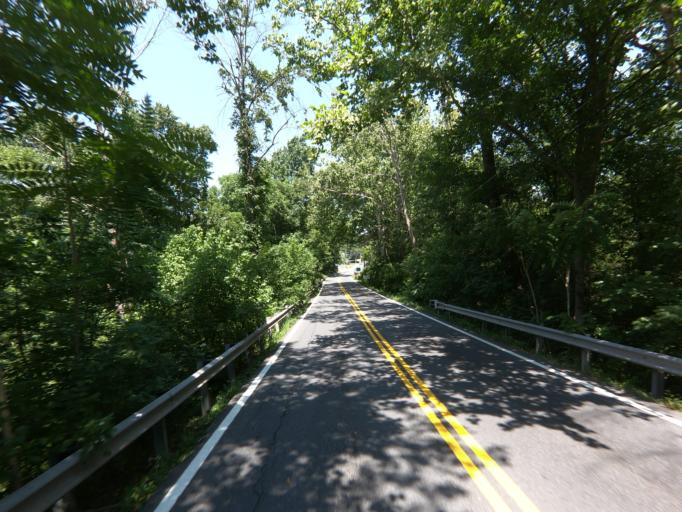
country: US
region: Maryland
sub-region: Frederick County
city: Green Valley
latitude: 39.2784
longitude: -77.3147
